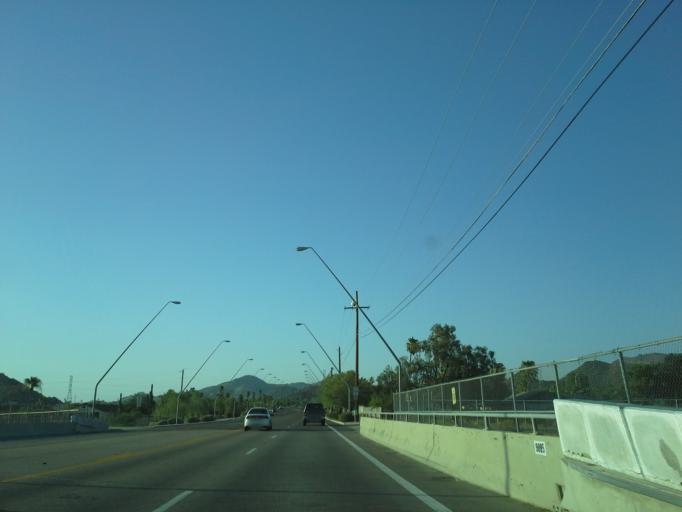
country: US
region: Arizona
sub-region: Pinal County
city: Apache Junction
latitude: 33.4256
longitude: -111.6326
